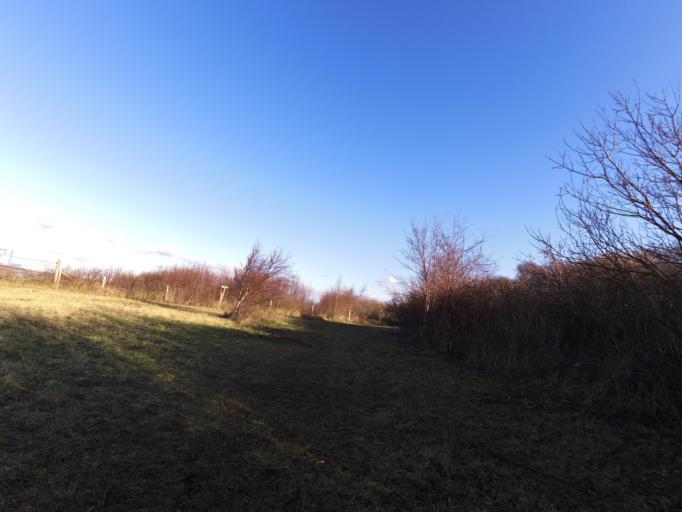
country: NL
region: South Holland
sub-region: Gemeente Rotterdam
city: Hoek van Holland
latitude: 51.9224
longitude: 4.0722
